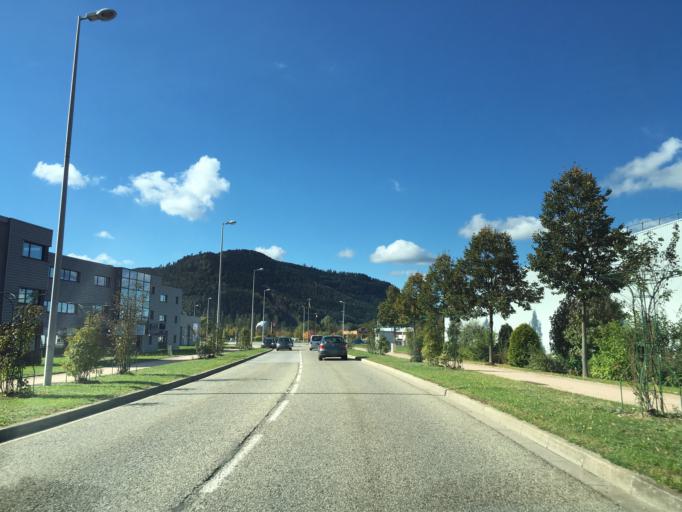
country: FR
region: Lorraine
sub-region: Departement des Vosges
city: Saint-Die-des-Vosges
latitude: 48.2925
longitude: 6.9366
